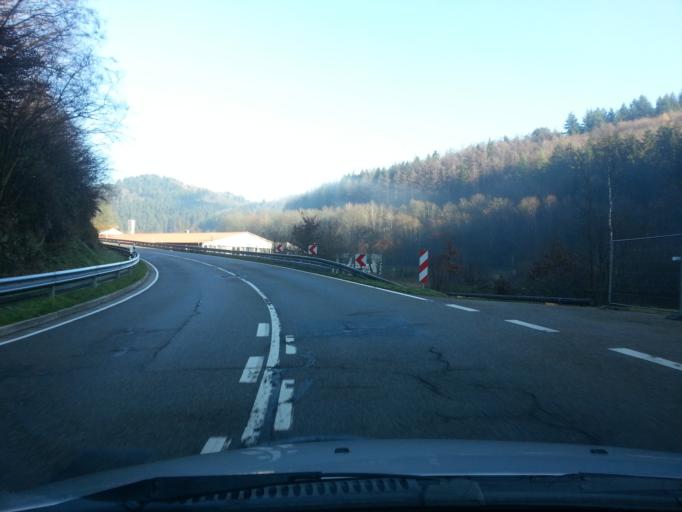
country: DE
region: Baden-Wuerttemberg
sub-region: Karlsruhe Region
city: Eberbach
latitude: 49.4861
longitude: 9.0414
